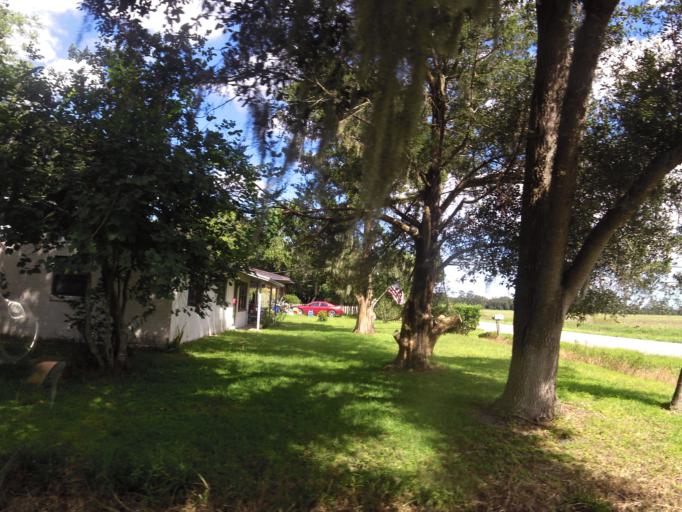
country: US
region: Florida
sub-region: Putnam County
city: East Palatka
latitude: 29.7108
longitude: -81.5060
